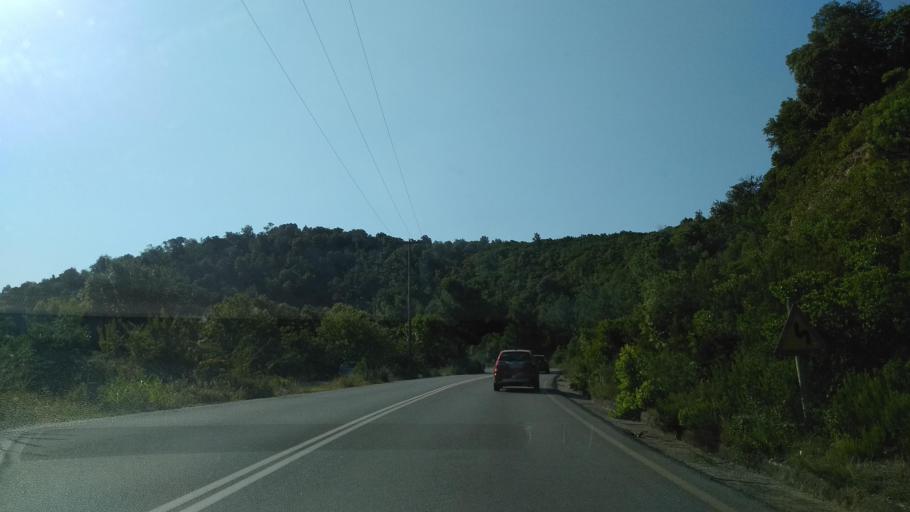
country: GR
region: Central Macedonia
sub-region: Nomos Chalkidikis
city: Stratonion
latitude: 40.5788
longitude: 23.8116
